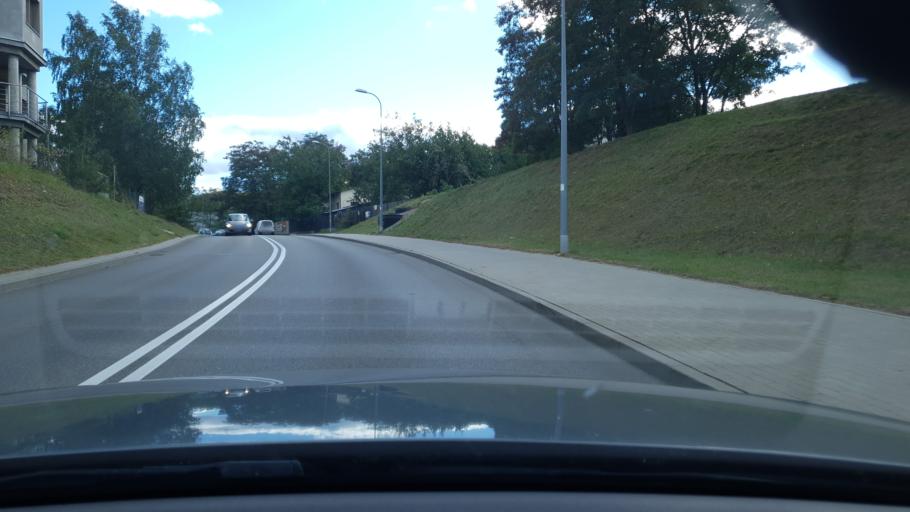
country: PL
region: Pomeranian Voivodeship
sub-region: Powiat wejherowski
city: Reda
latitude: 54.6009
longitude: 18.3446
